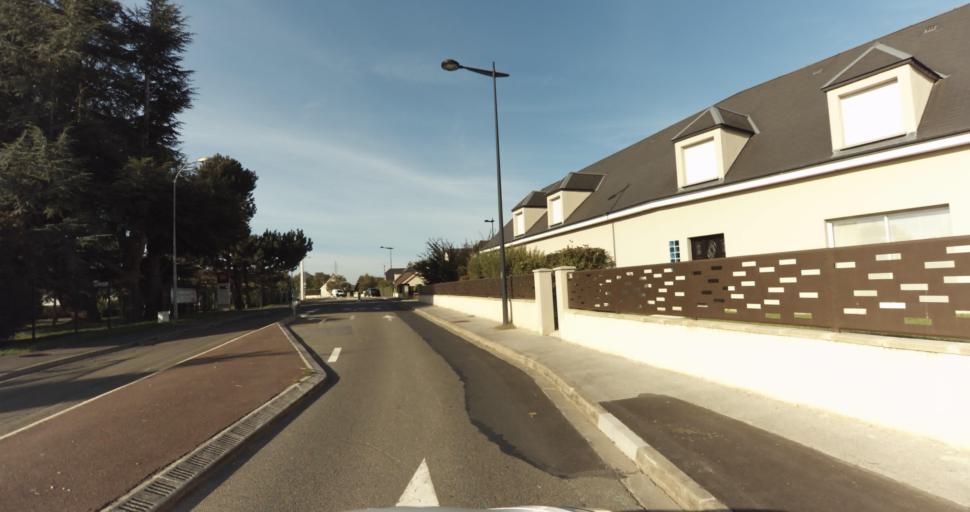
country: FR
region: Champagne-Ardenne
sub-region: Departement des Ardennes
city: Villers-Semeuse
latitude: 49.7374
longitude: 4.7446
